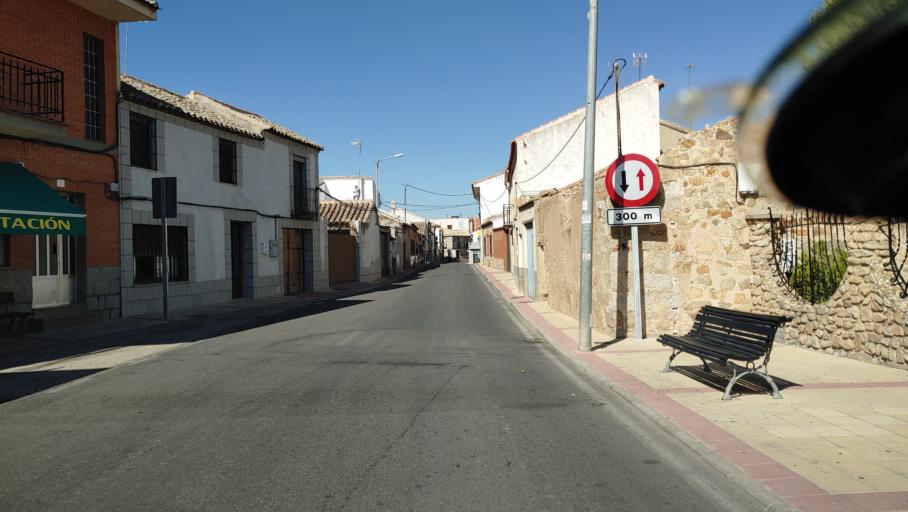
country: ES
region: Castille-La Mancha
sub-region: Province of Toledo
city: Pulgar
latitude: 39.6929
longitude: -4.1545
